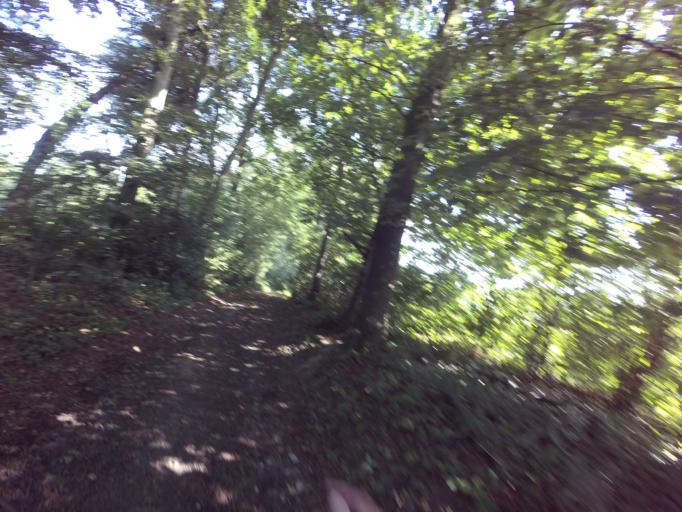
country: BE
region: Wallonia
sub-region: Province de Liege
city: Plombieres
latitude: 50.7393
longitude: 5.9510
